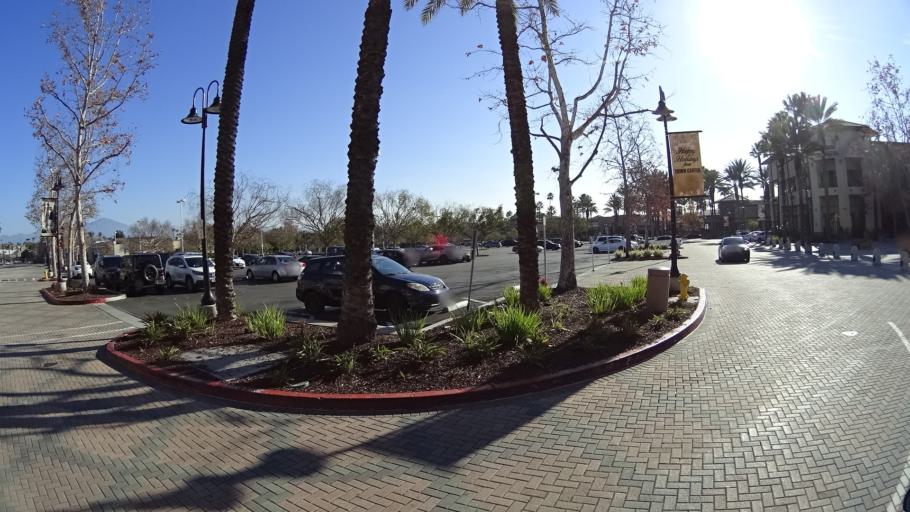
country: US
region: California
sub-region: Orange County
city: Aliso Viejo
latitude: 33.5761
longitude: -117.7266
